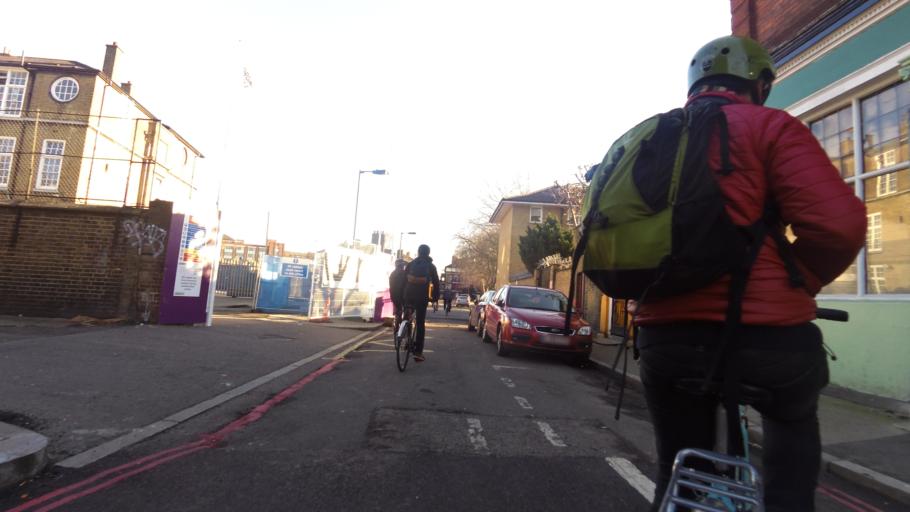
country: GB
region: England
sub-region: Greater London
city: City of London
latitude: 51.4959
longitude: -0.0828
